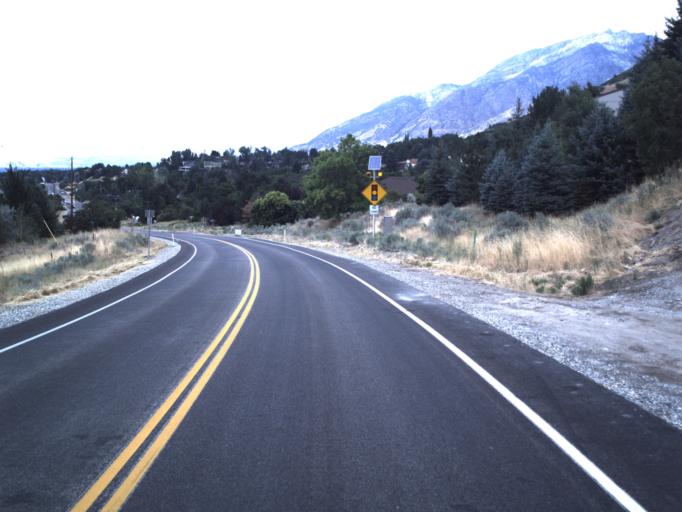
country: US
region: Utah
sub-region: Salt Lake County
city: Granite
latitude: 40.5860
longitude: -111.7921
